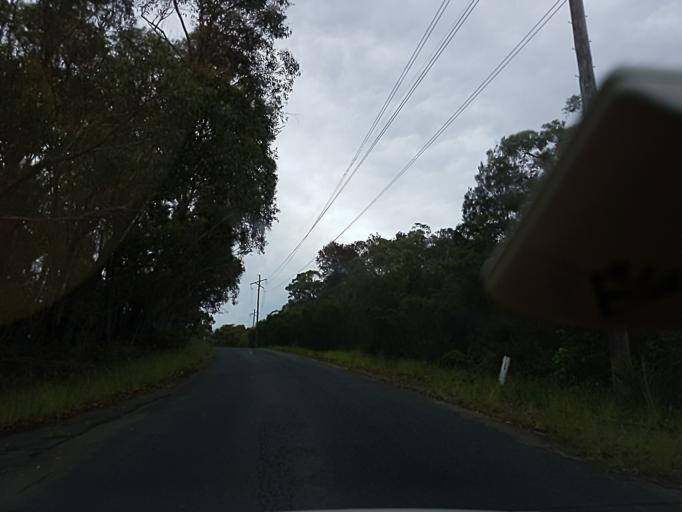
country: AU
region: New South Wales
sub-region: Warringah
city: Davidson
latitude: -33.7255
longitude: 151.2306
